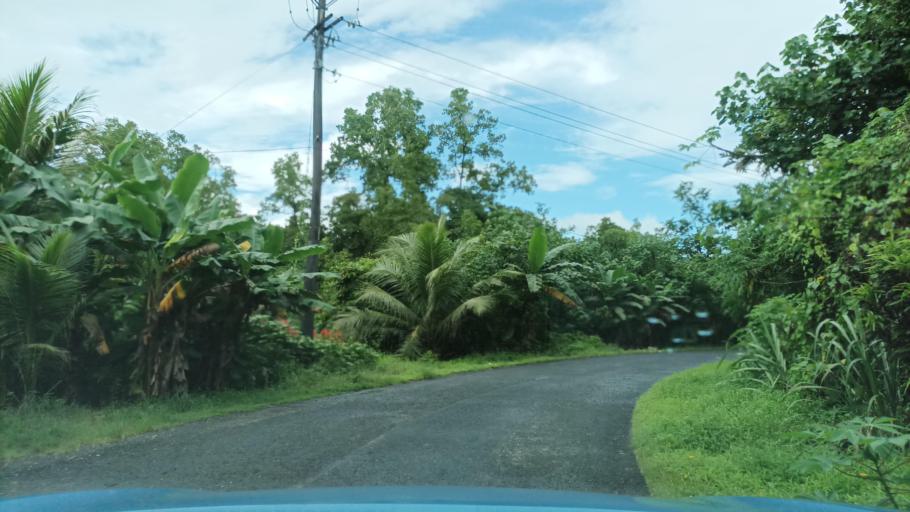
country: FM
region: Pohnpei
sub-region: Sokehs Municipality
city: Palikir - National Government Center
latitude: 6.8269
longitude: 158.1547
